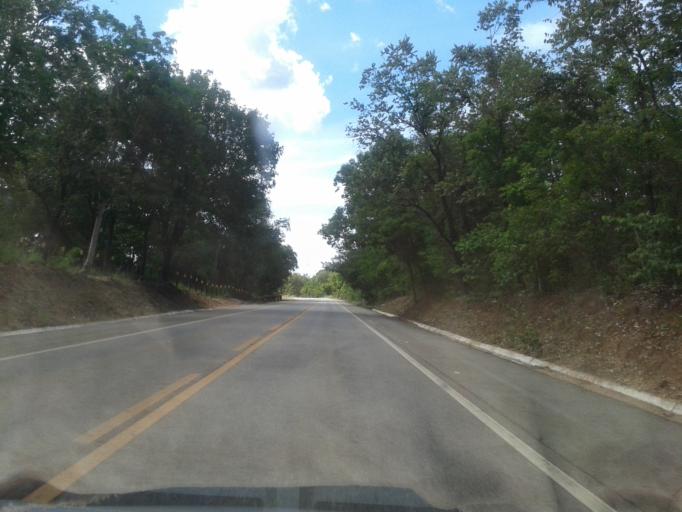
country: BR
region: Goias
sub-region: Itapuranga
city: Itapuranga
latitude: -15.4974
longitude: -50.3085
